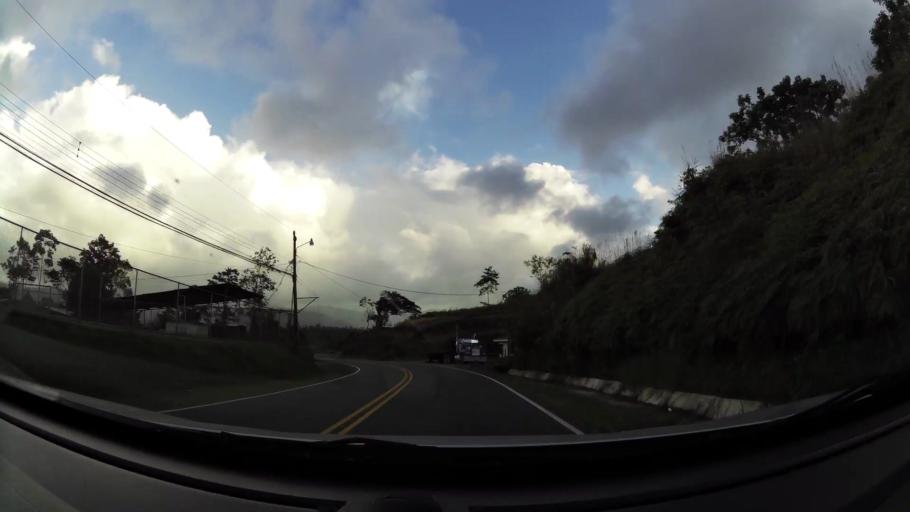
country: CR
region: Limon
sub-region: Canton de Siquirres
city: Siquirres
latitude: 9.9881
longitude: -83.5707
